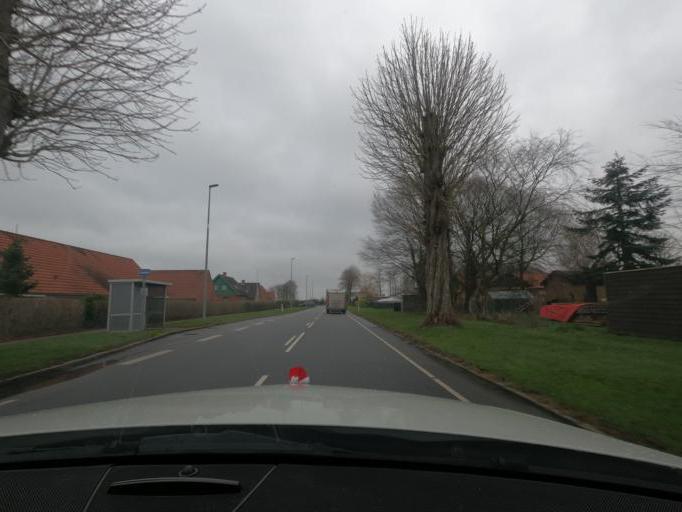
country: DK
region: South Denmark
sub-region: Haderslev Kommune
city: Starup
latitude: 55.2585
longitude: 9.7078
